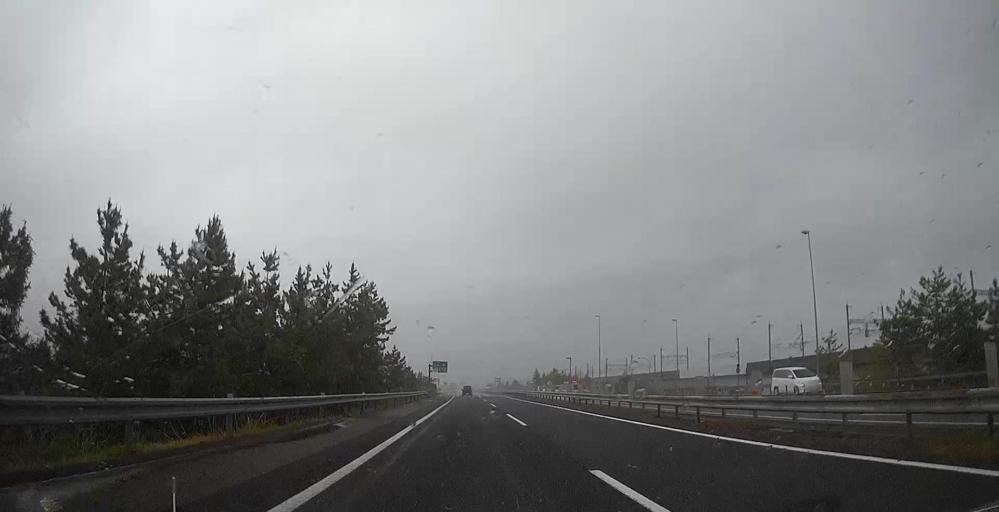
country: JP
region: Niigata
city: Tsubame
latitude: 37.6510
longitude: 138.9392
